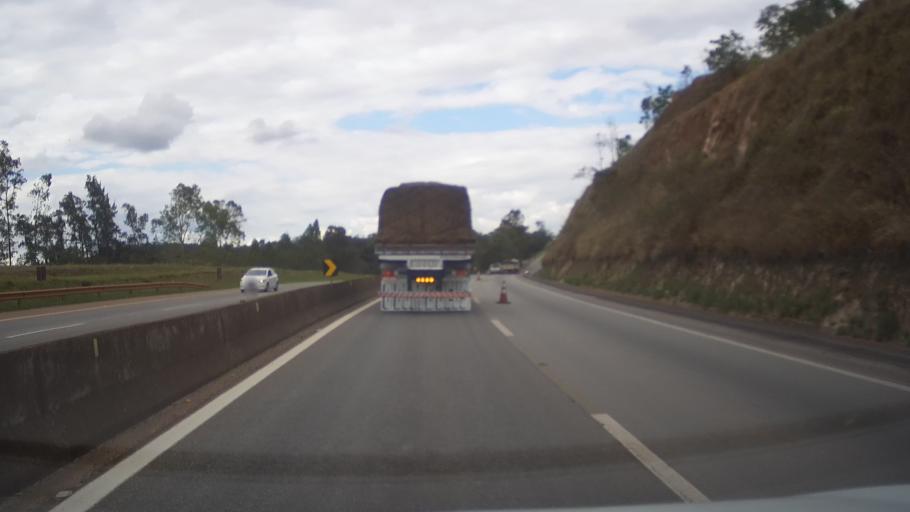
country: BR
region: Minas Gerais
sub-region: Itauna
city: Itauna
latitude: -20.3223
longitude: -44.4565
